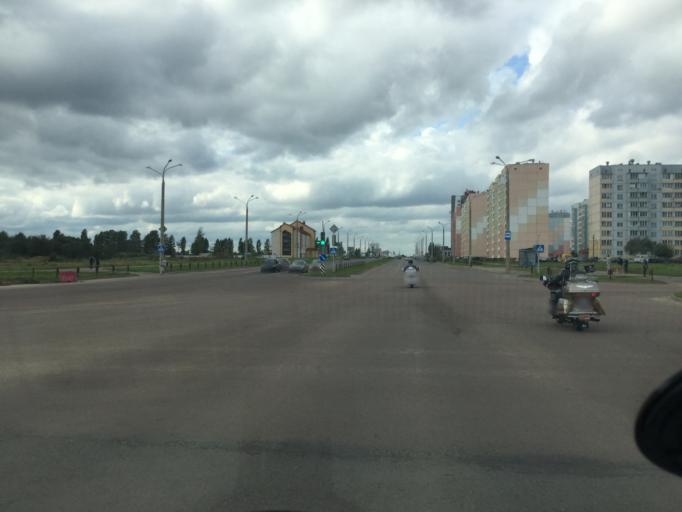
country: BY
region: Vitebsk
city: Vitebsk
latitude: 55.1651
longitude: 30.2654
